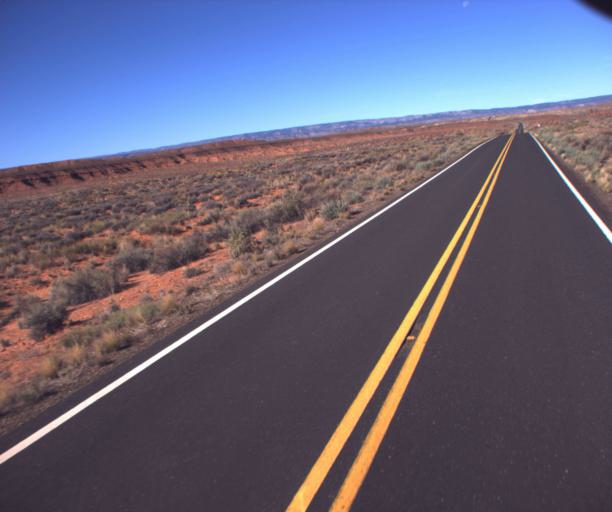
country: US
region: Arizona
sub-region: Coconino County
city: Page
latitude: 36.6859
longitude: -111.8627
